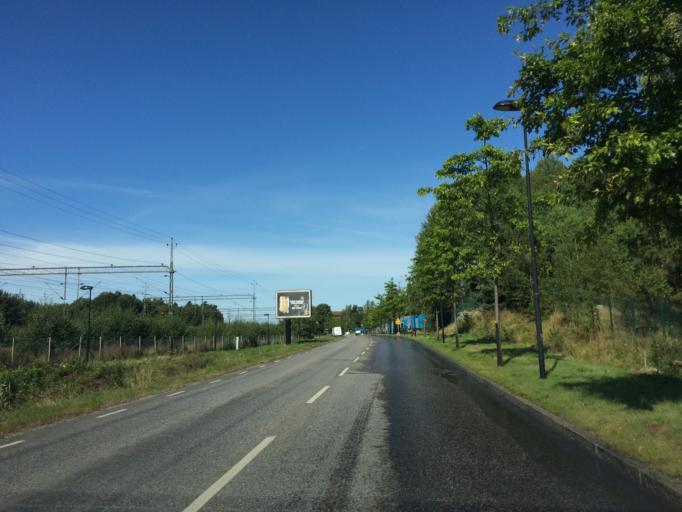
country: SE
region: Stockholm
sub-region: Solna Kommun
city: Rasunda
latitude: 59.3968
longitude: 17.9852
